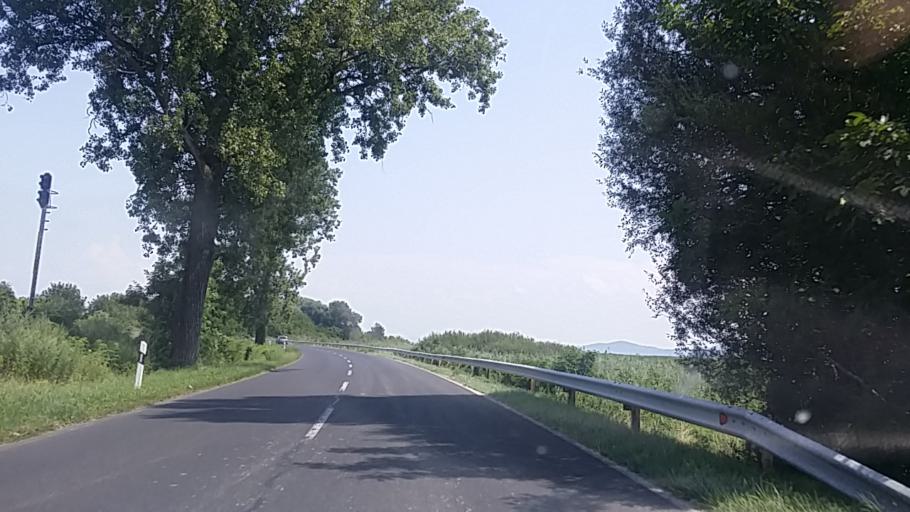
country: HU
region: Veszprem
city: Badacsonytomaj
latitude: 46.7863
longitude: 17.4845
